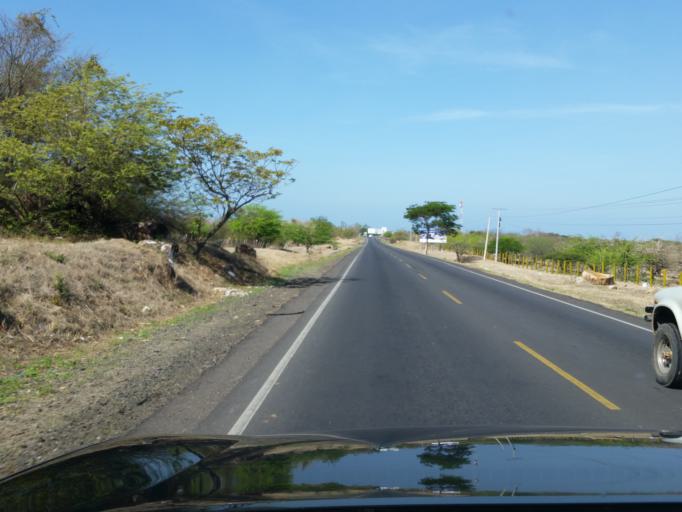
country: NI
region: Leon
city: La Paz Centro
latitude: 12.2728
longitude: -86.7318
